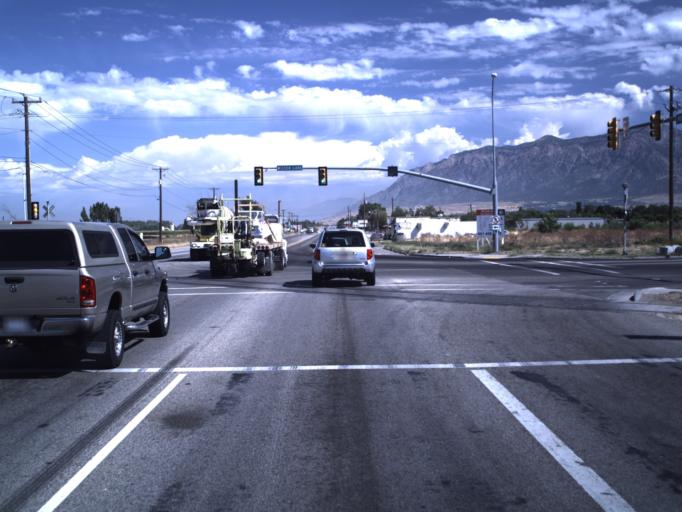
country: US
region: Utah
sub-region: Weber County
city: Marriott-Slaterville
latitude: 41.2283
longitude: -112.0255
